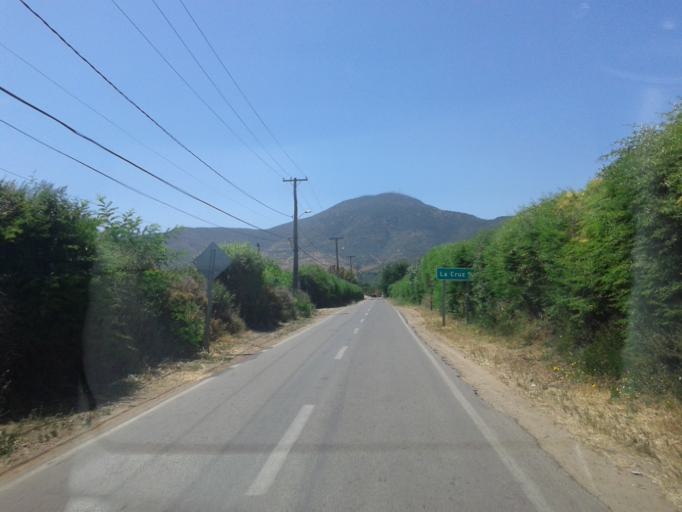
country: CL
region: Valparaiso
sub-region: Provincia de Quillota
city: Quillota
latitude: -32.8495
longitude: -71.1902
